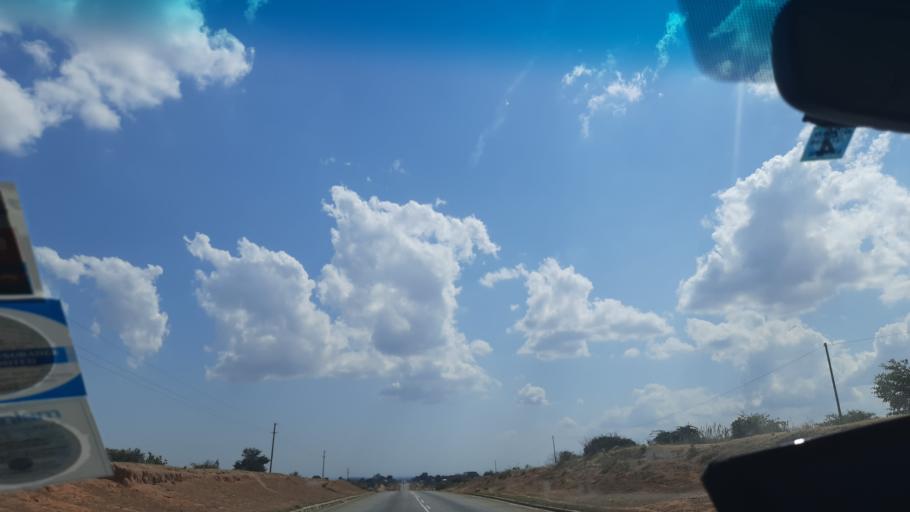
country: TZ
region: Singida
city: Kintinku
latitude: -6.0166
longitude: 35.4453
